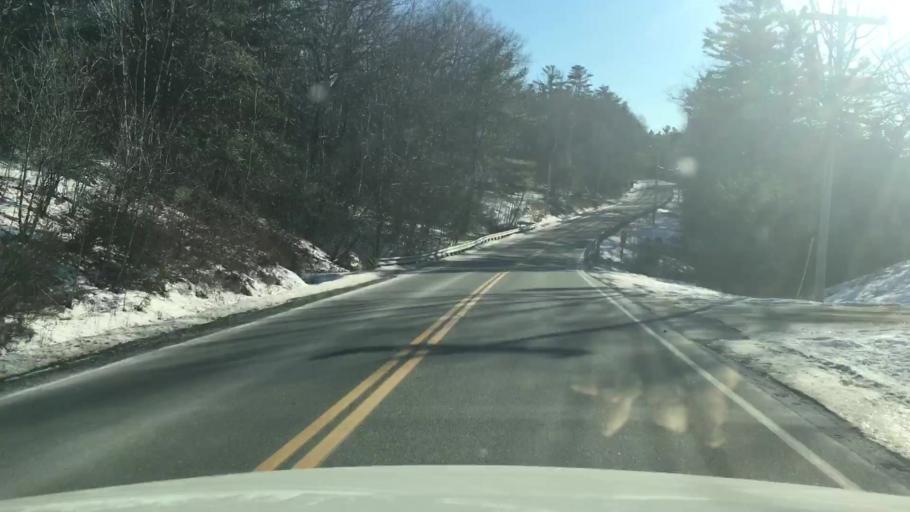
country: US
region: Maine
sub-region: Hancock County
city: Orland
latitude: 44.5416
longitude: -68.7453
